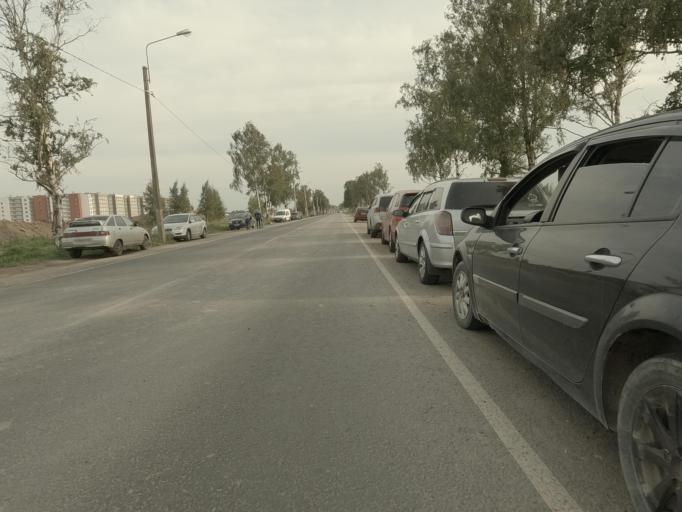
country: RU
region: St.-Petersburg
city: Strel'na
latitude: 59.8462
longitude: 30.0909
